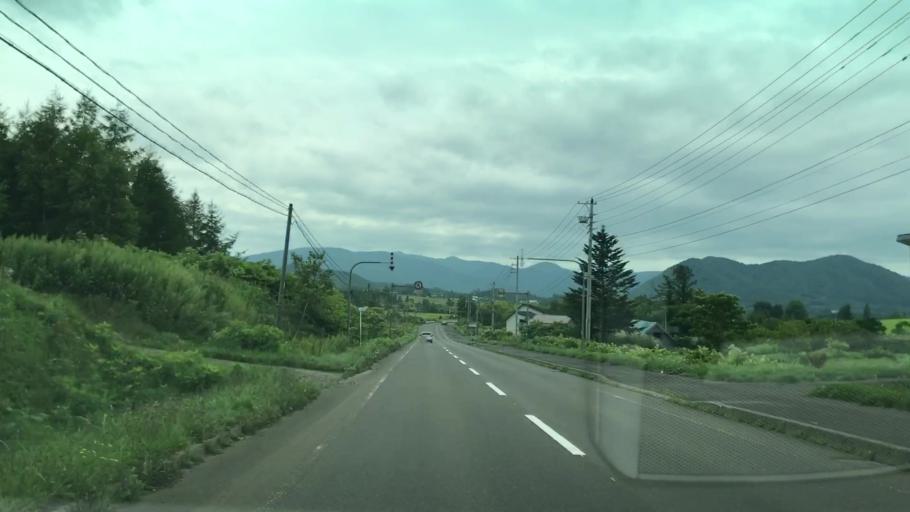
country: JP
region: Hokkaido
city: Yoichi
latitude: 43.1027
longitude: 140.8236
